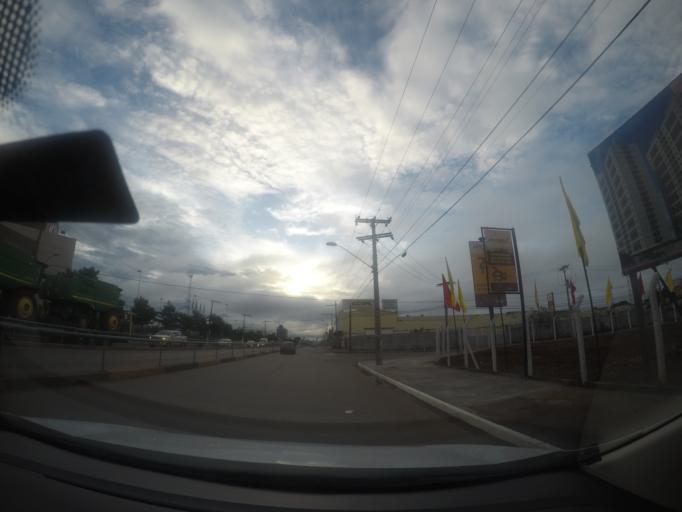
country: BR
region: Goias
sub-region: Goiania
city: Goiania
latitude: -16.6672
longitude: -49.3097
